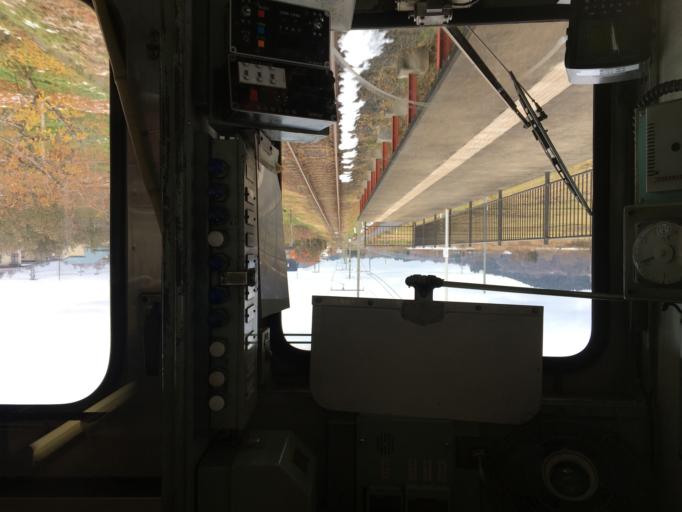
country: JP
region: Aomori
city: Hirosaki
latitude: 40.5252
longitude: 140.5576
